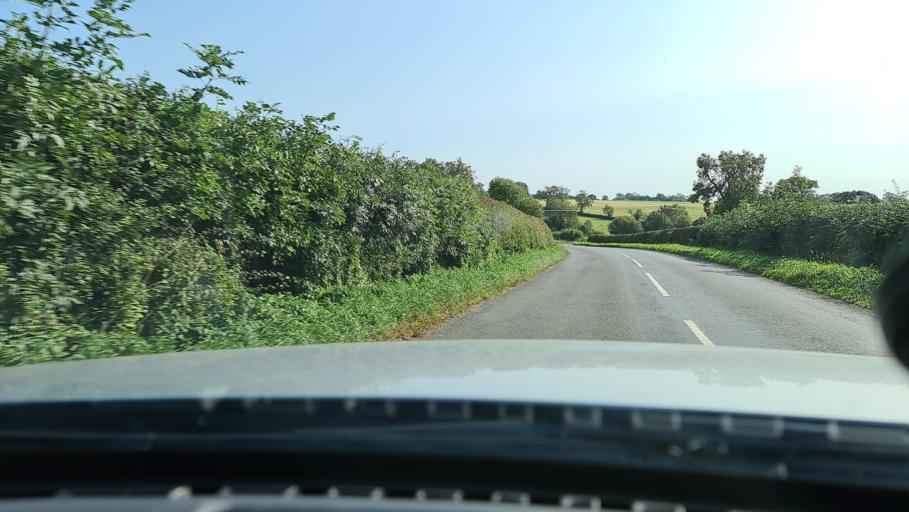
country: GB
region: England
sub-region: Northamptonshire
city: Daventry
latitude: 52.1616
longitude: -1.1208
